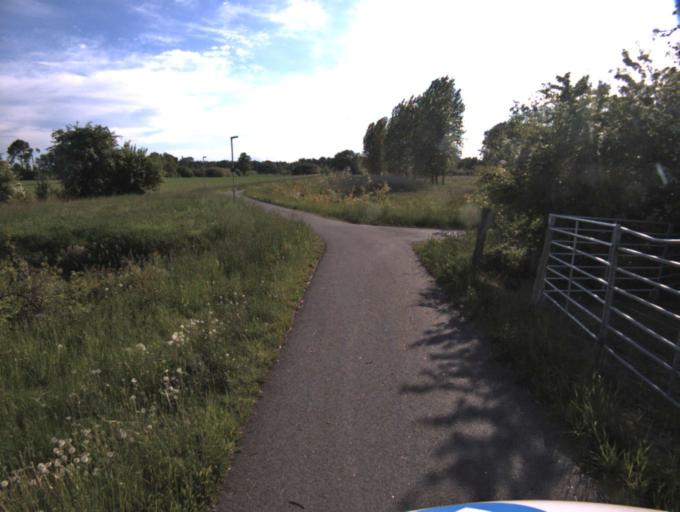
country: SE
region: Skane
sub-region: Kristianstads Kommun
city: Kristianstad
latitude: 56.0472
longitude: 14.1983
